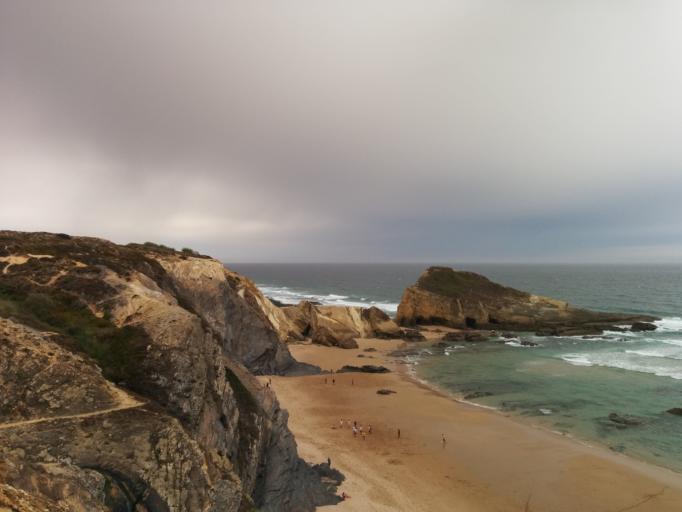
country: PT
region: Beja
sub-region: Odemira
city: Sao Teotonio
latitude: 37.5188
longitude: -8.7878
